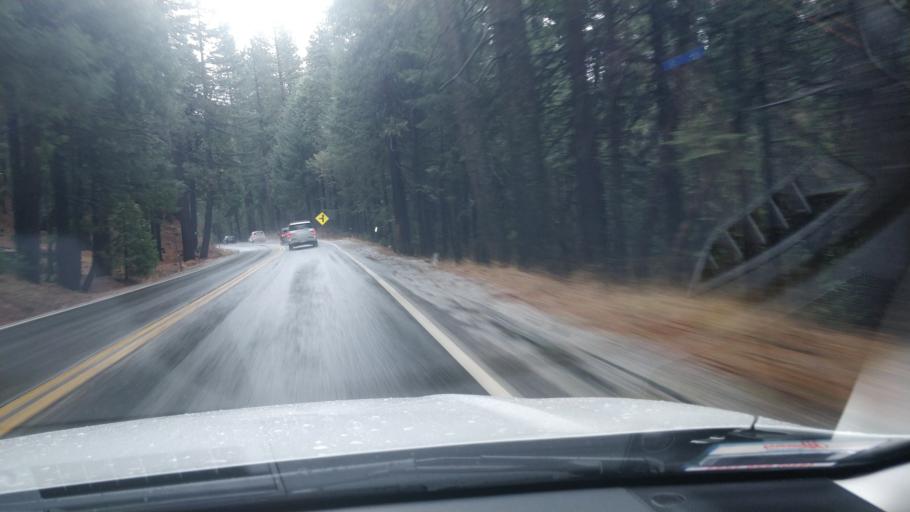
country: US
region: California
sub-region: Nevada County
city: Nevada City
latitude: 39.3200
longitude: -120.7899
